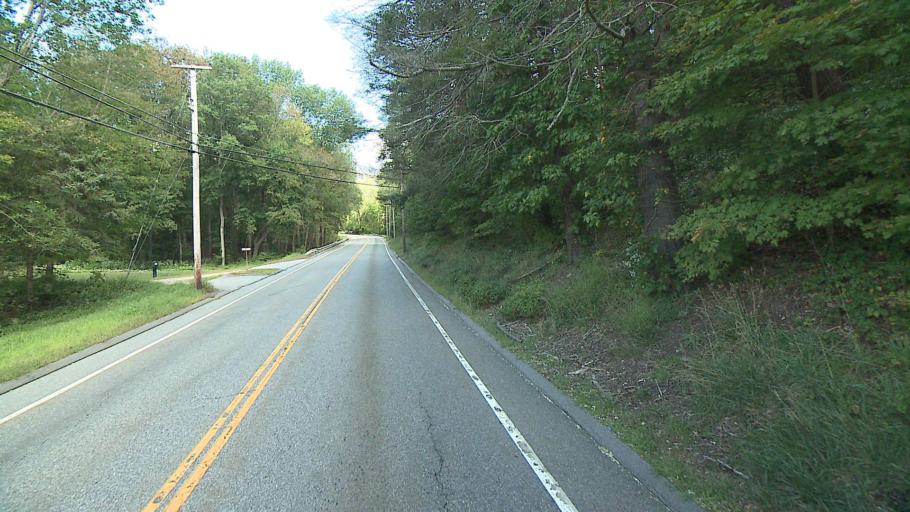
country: US
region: Connecticut
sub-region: Windham County
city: South Woodstock
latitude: 41.8751
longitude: -71.9618
